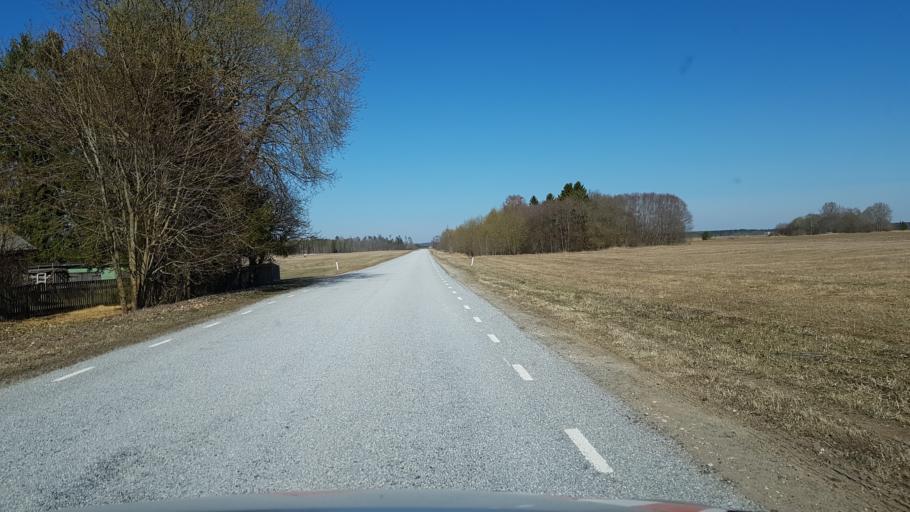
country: EE
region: Jaervamaa
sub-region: Koeru vald
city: Koeru
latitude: 59.0150
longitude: 26.0884
